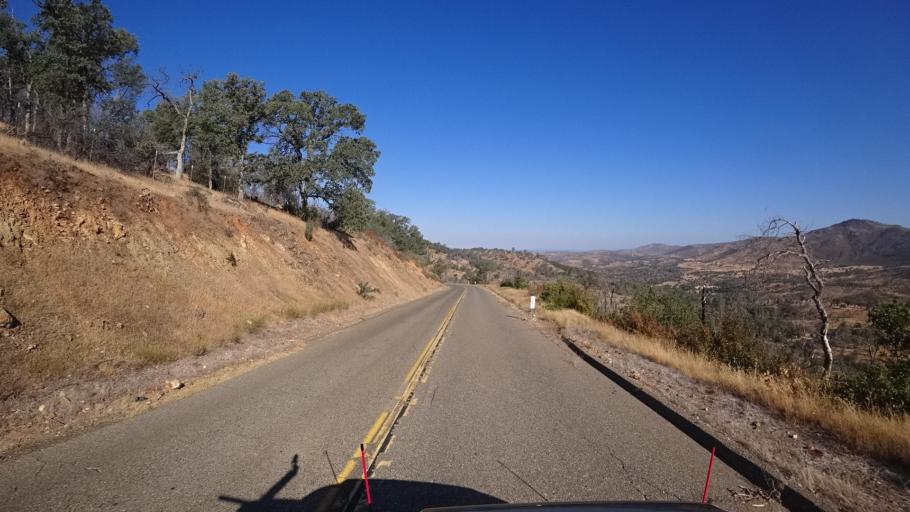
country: US
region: California
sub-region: Mariposa County
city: Mariposa
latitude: 37.5643
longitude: -120.1637
